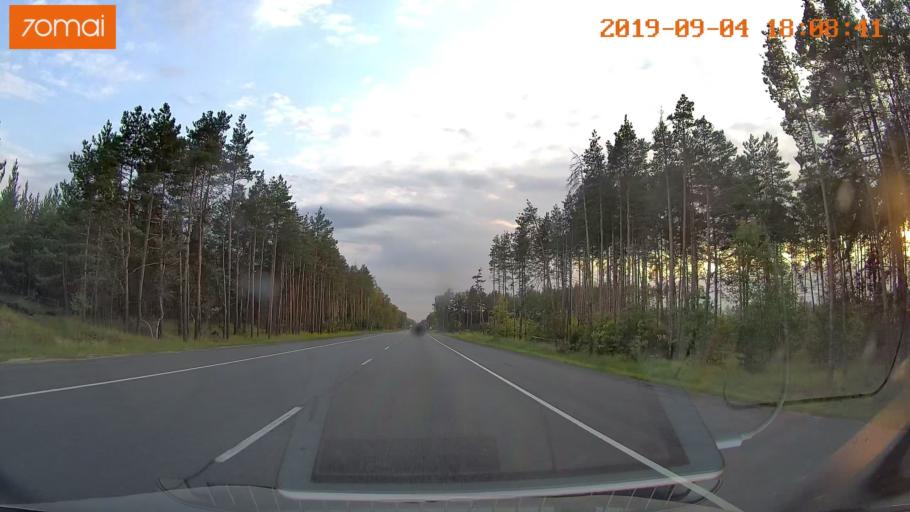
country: RU
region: Moskovskaya
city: Khorlovo
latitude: 55.4030
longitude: 38.7826
